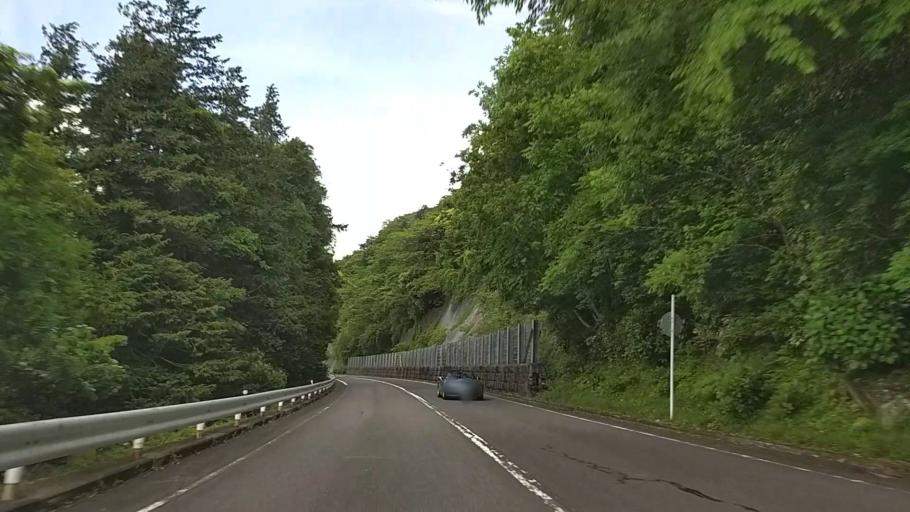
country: JP
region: Kanagawa
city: Odawara
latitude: 35.2367
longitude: 139.1270
